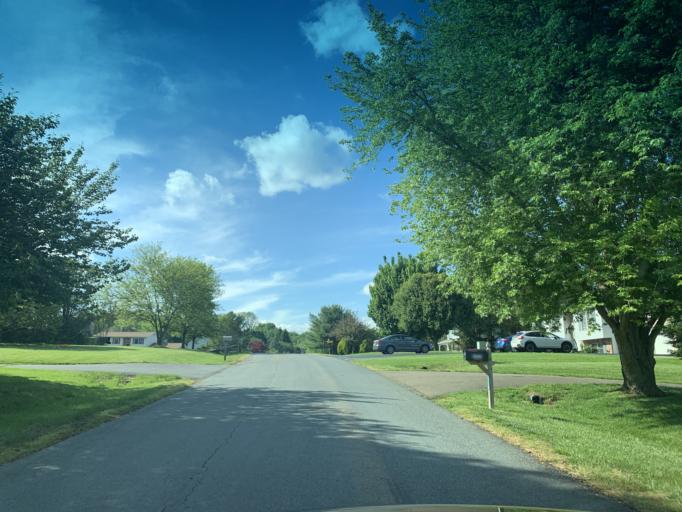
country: US
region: Maryland
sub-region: Cecil County
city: Rising Sun
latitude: 39.6939
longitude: -76.1439
